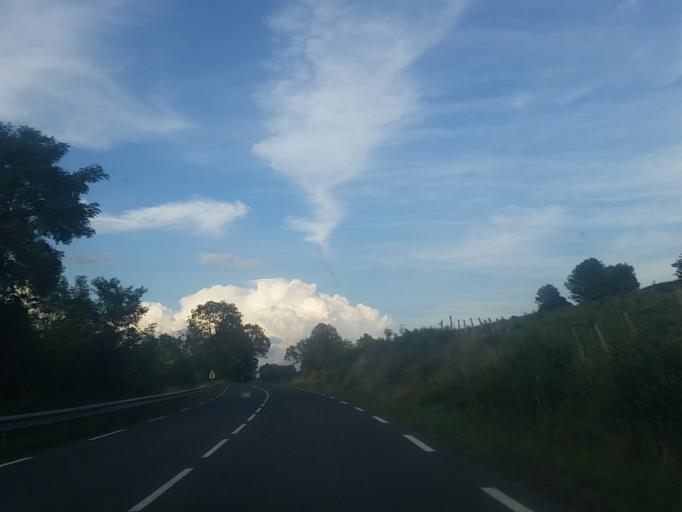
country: FR
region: Auvergne
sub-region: Departement du Cantal
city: Pierrefort
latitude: 44.9347
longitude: 2.8549
